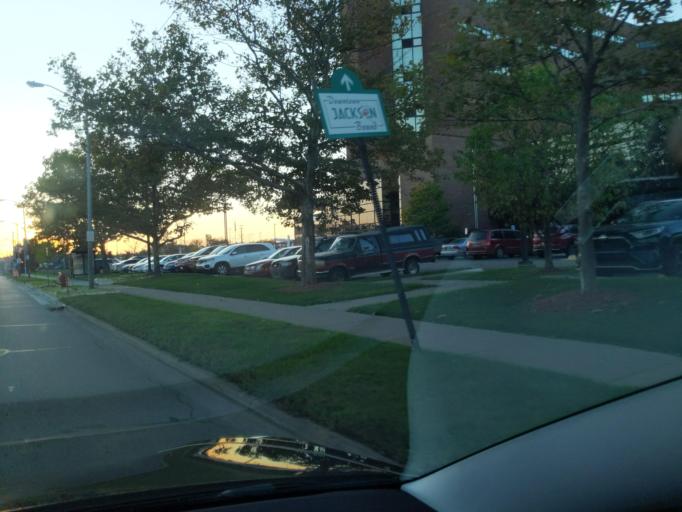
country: US
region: Michigan
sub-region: Jackson County
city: Jackson
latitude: 42.2501
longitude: -84.3916
